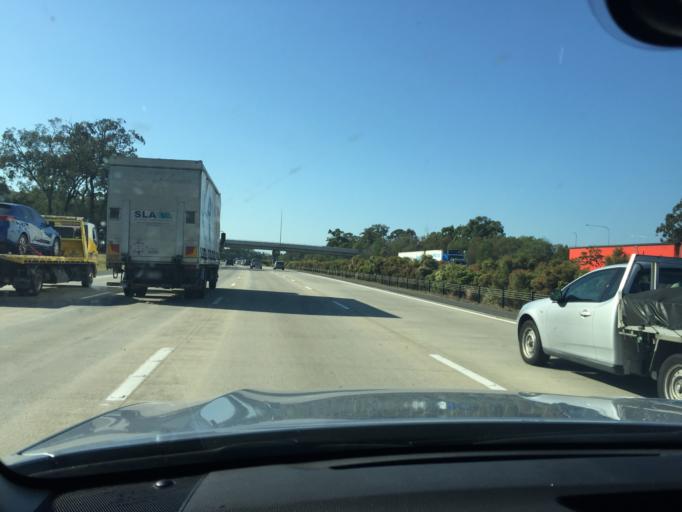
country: AU
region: Queensland
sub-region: Gold Coast
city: Ormeau Hills
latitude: -27.7569
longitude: 153.2406
